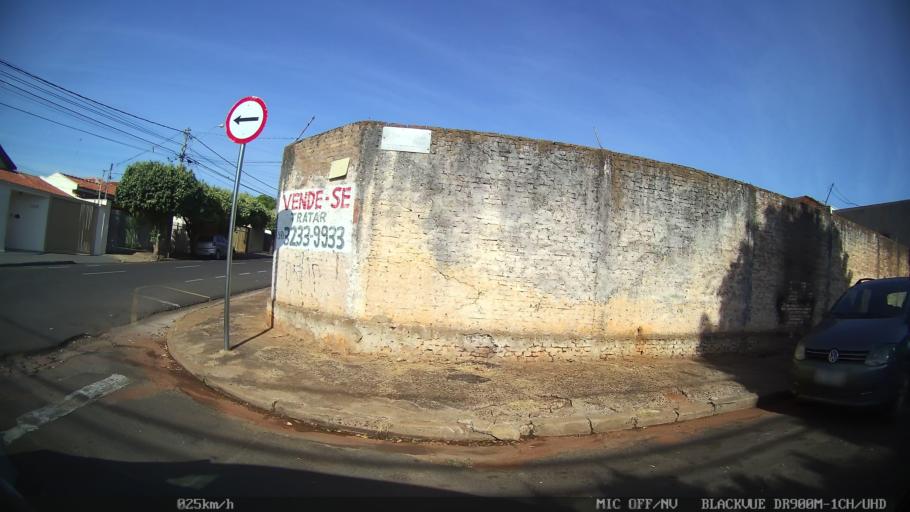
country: BR
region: Sao Paulo
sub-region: Sao Jose Do Rio Preto
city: Sao Jose do Rio Preto
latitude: -20.8000
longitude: -49.3931
